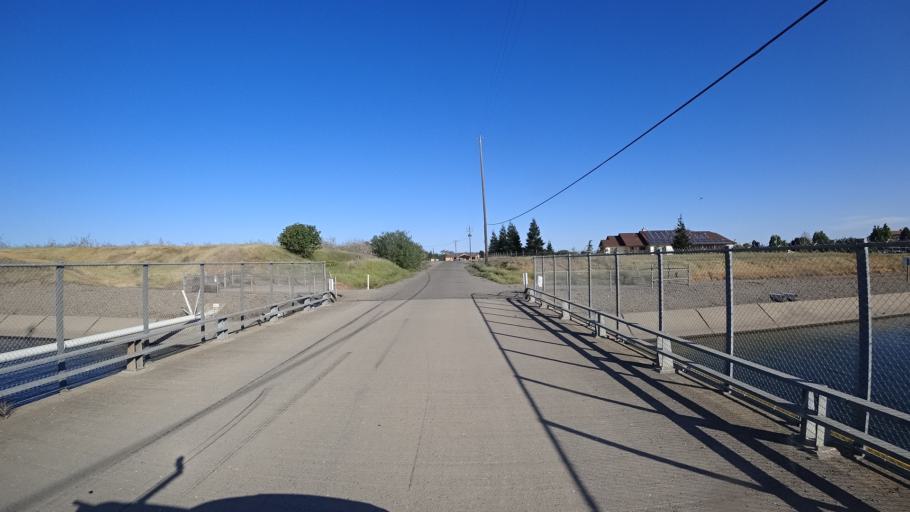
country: US
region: California
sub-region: Glenn County
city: Orland
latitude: 39.7193
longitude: -122.1726
